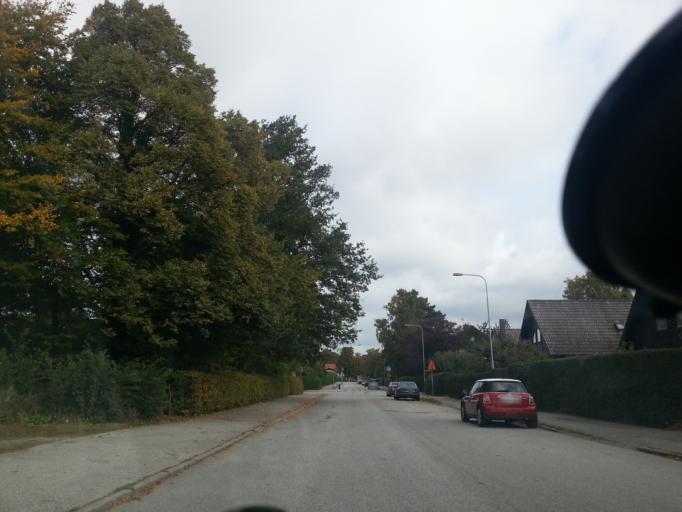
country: SE
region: Skane
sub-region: Lunds Kommun
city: Lund
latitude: 55.6923
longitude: 13.1995
